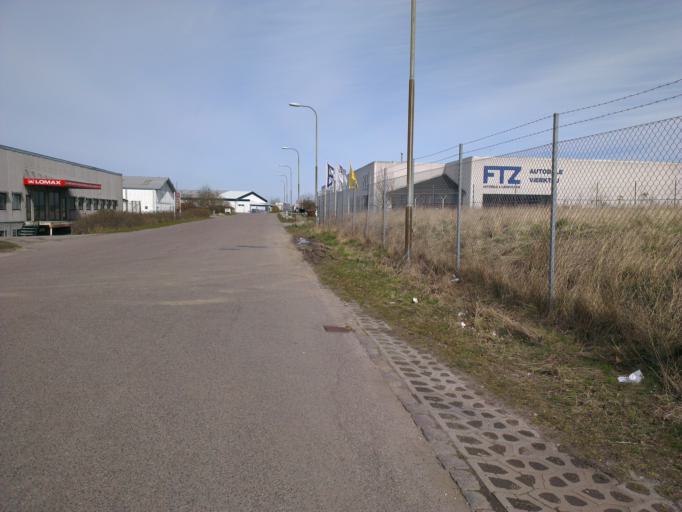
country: DK
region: Capital Region
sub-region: Frederikssund Kommune
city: Frederikssund
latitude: 55.8498
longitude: 12.0675
